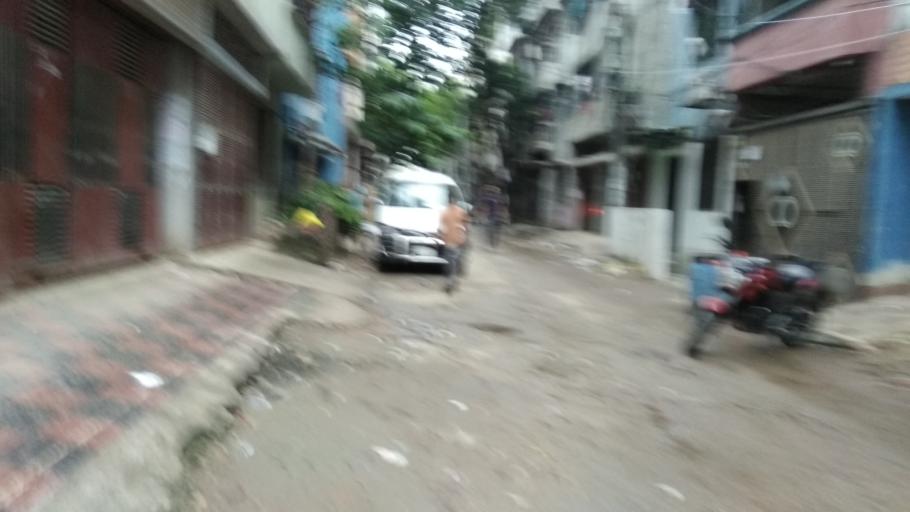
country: BD
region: Dhaka
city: Tungi
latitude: 23.8253
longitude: 90.3697
